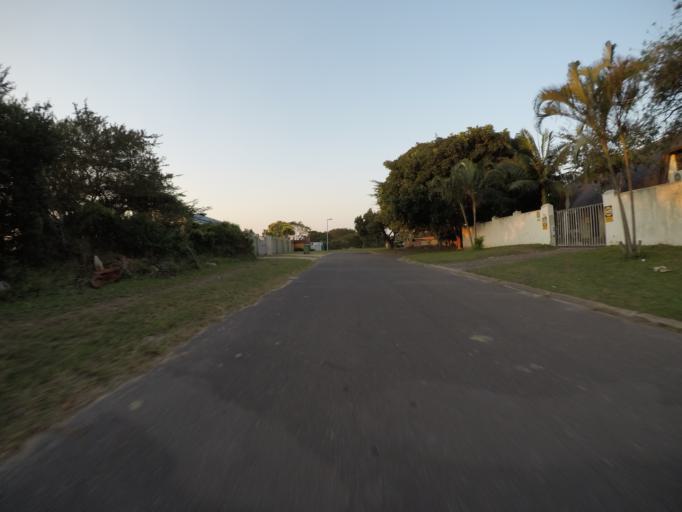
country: ZA
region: KwaZulu-Natal
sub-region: uThungulu District Municipality
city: Richards Bay
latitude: -28.7676
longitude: 32.1252
